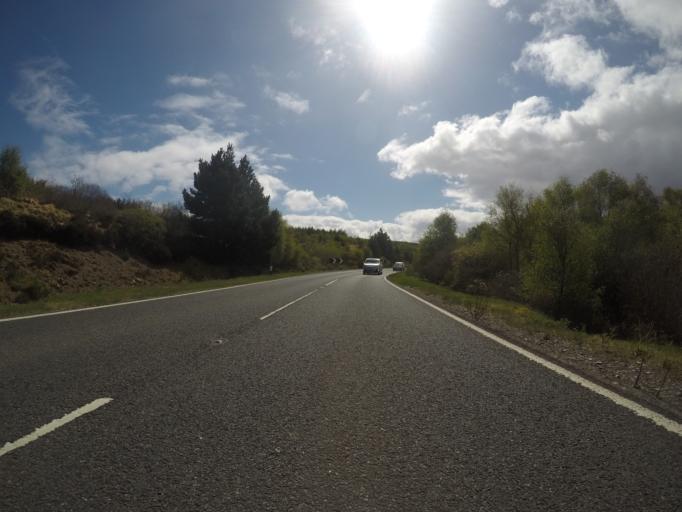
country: GB
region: Scotland
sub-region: Highland
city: Isle of Skye
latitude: 57.3441
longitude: -6.1975
